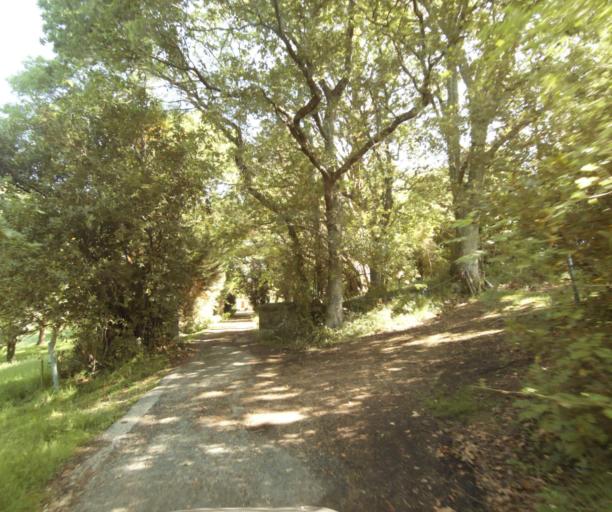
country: FR
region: Aquitaine
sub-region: Departement des Pyrenees-Atlantiques
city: Mouguerre
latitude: 43.4726
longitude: -1.4397
